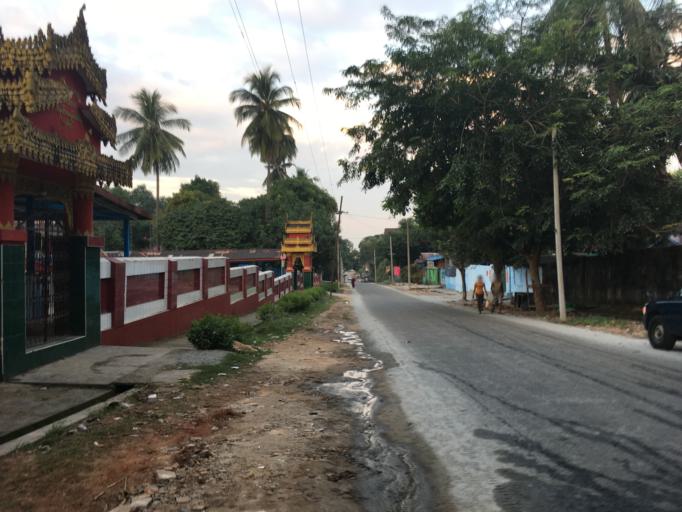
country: MM
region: Mon
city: Mawlamyine
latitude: 16.4853
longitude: 97.6260
